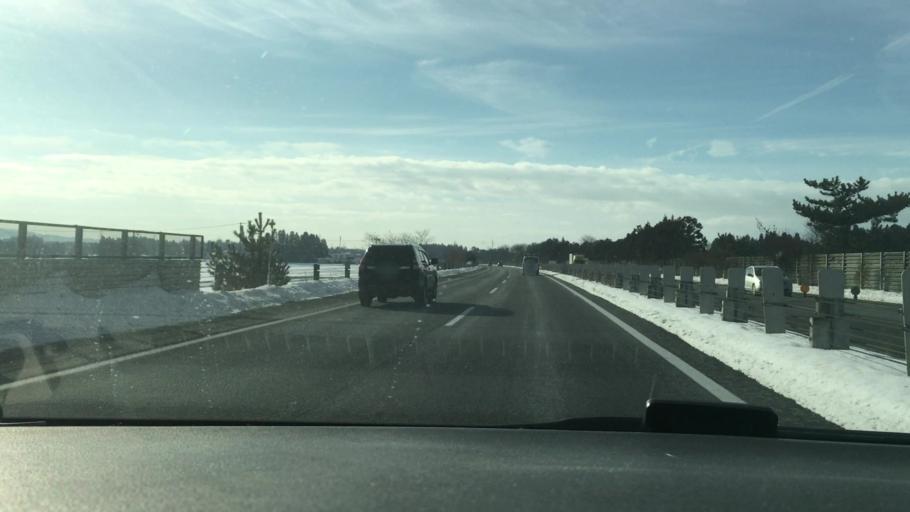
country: JP
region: Iwate
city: Hanamaki
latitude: 39.3591
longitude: 141.0897
